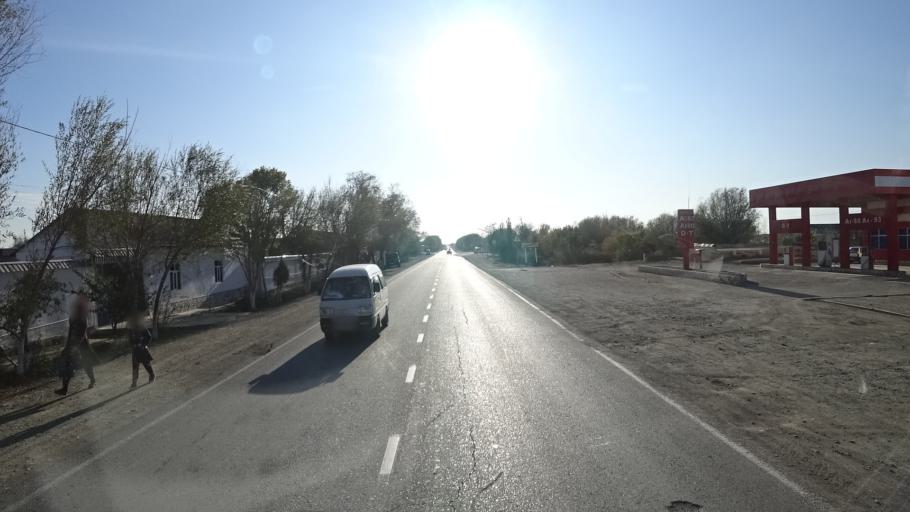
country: UZ
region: Navoiy
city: Beshrabot
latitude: 40.2003
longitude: 65.3767
